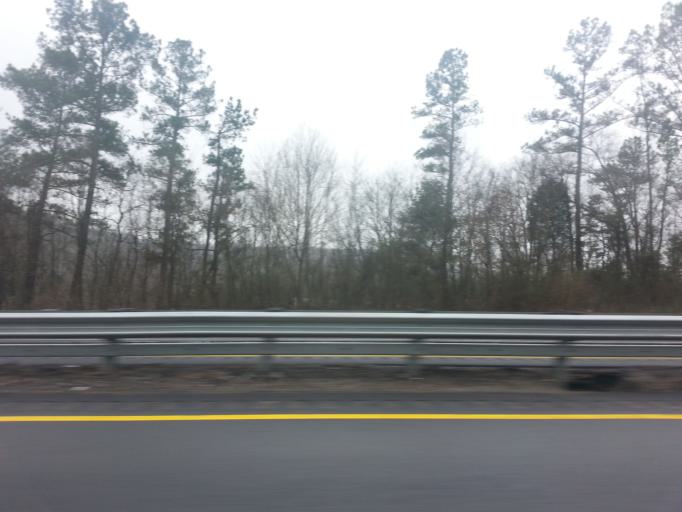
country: US
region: Tennessee
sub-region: Roane County
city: Kingston
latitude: 35.8949
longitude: -84.5355
